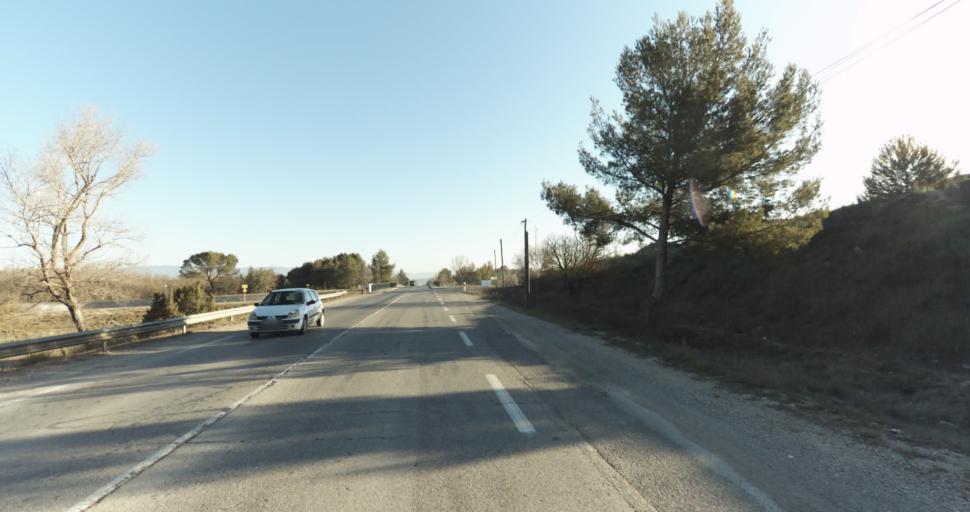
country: FR
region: Provence-Alpes-Cote d'Azur
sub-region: Departement des Bouches-du-Rhone
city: Venelles
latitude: 43.6347
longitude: 5.4877
